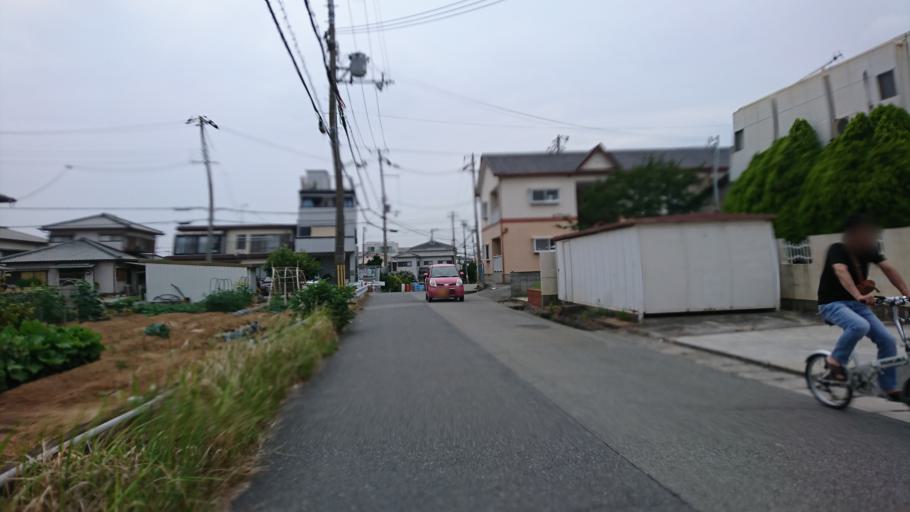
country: JP
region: Hyogo
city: Kakogawacho-honmachi
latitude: 34.7270
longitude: 134.8997
